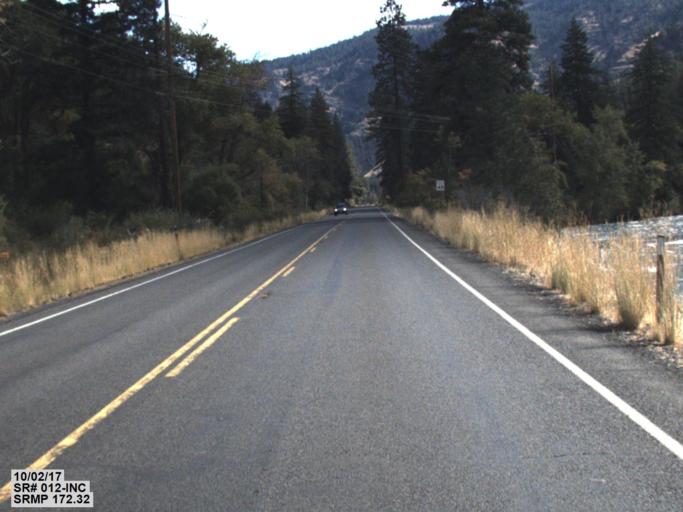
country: US
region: Washington
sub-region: Yakima County
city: Tieton
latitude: 46.6715
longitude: -120.9996
